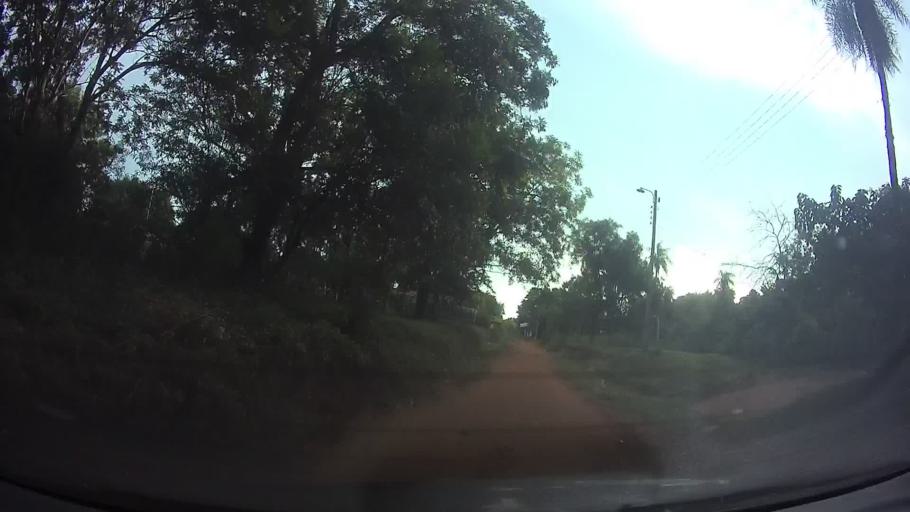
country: PY
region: Central
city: Limpio
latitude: -25.2428
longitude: -57.4488
